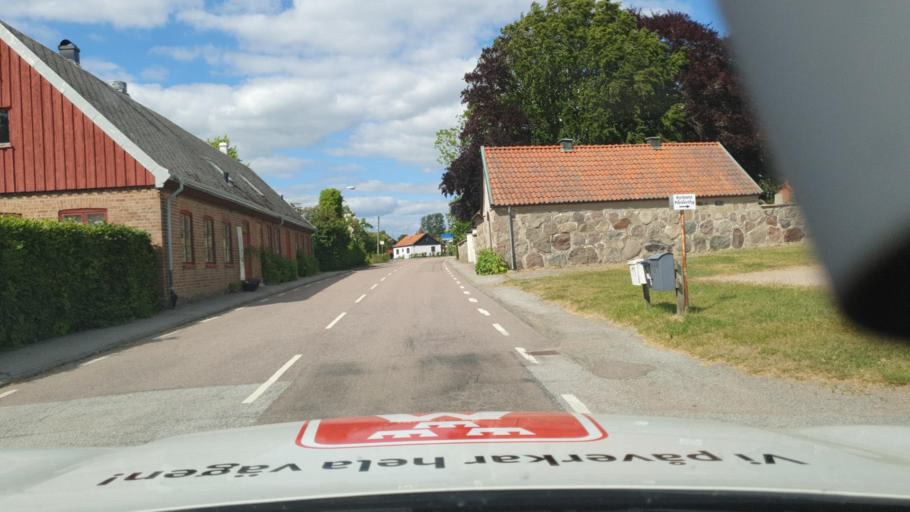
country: SE
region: Skane
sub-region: Ystads Kommun
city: Kopingebro
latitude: 55.4704
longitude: 13.9457
